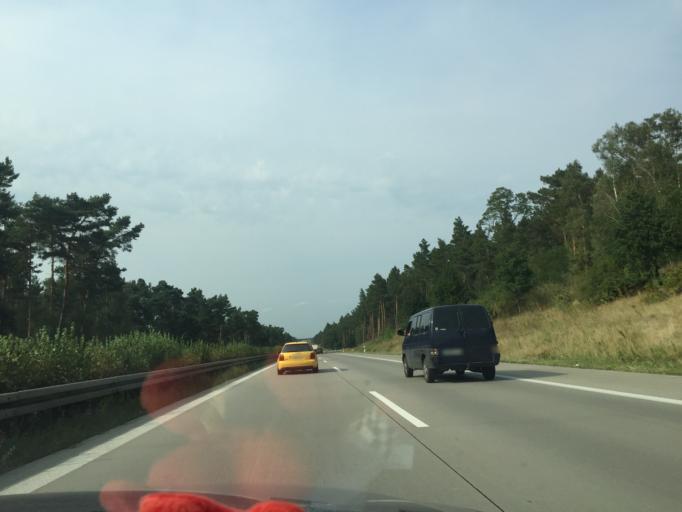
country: DE
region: Brandenburg
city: Teupitz
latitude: 52.0871
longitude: 13.6489
